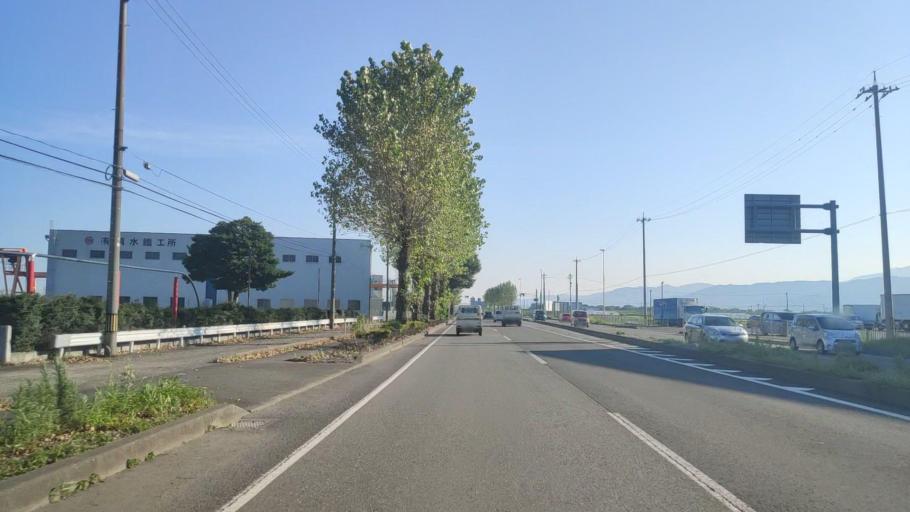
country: JP
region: Fukui
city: Fukui-shi
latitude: 36.1004
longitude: 136.2535
